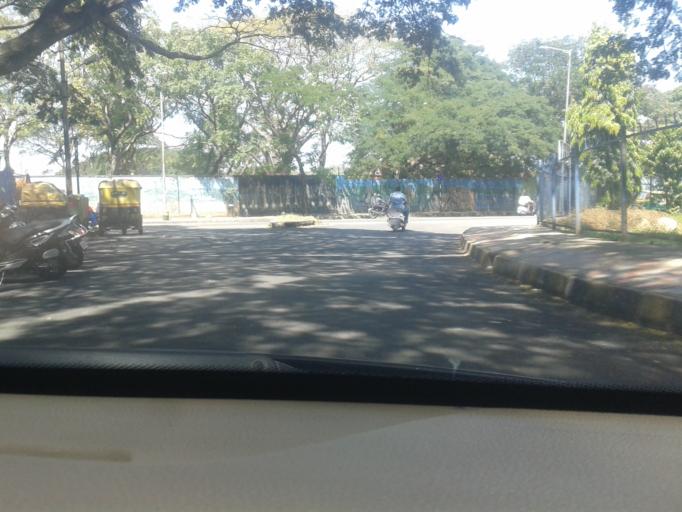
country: IN
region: Karnataka
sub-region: Bangalore Urban
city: Bangalore
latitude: 12.9456
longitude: 77.5870
